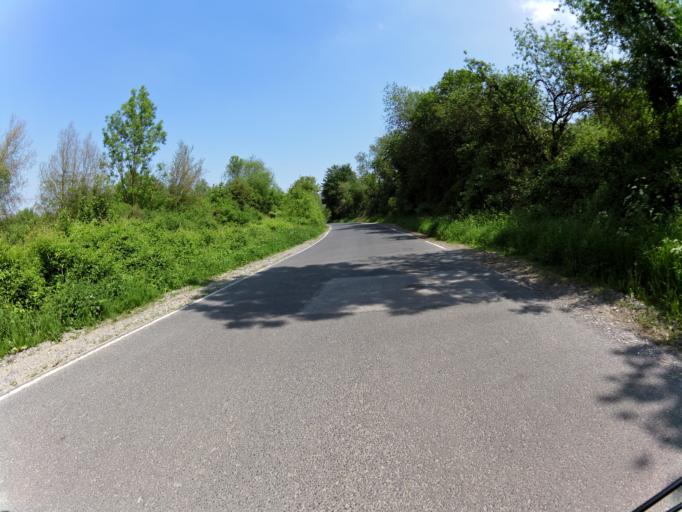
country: DE
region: North Rhine-Westphalia
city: Julich
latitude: 50.9082
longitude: 6.3672
